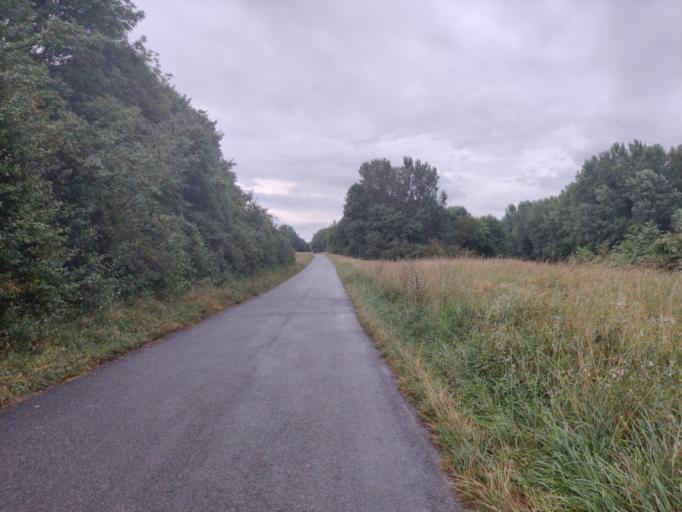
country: AT
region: Lower Austria
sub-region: Politischer Bezirk Korneuburg
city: Langenzersdorf
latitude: 48.2955
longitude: 16.3480
